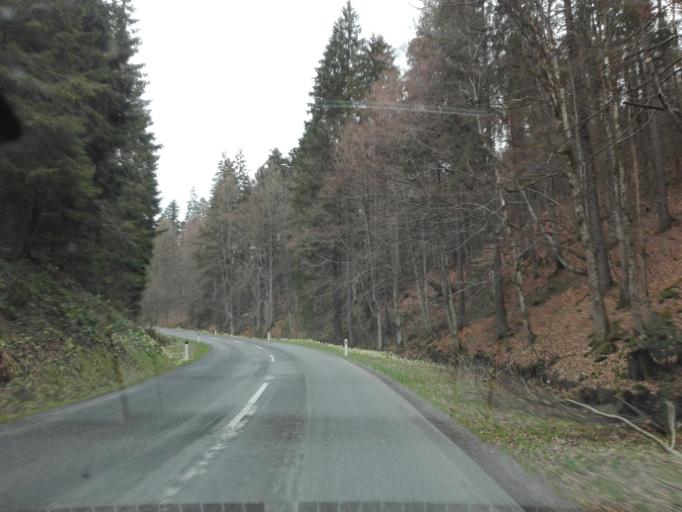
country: AT
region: Upper Austria
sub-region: Politischer Bezirk Rohrbach
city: Ulrichsberg
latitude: 48.7252
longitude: 13.8901
